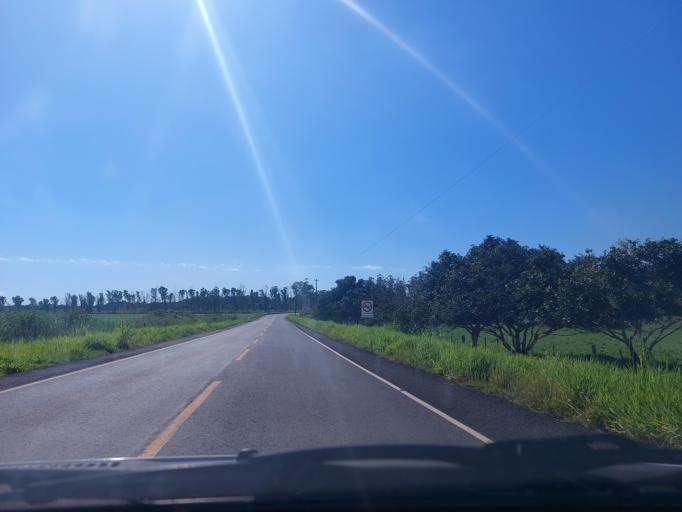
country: PY
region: San Pedro
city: Guayaybi
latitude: -24.3194
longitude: -56.1828
